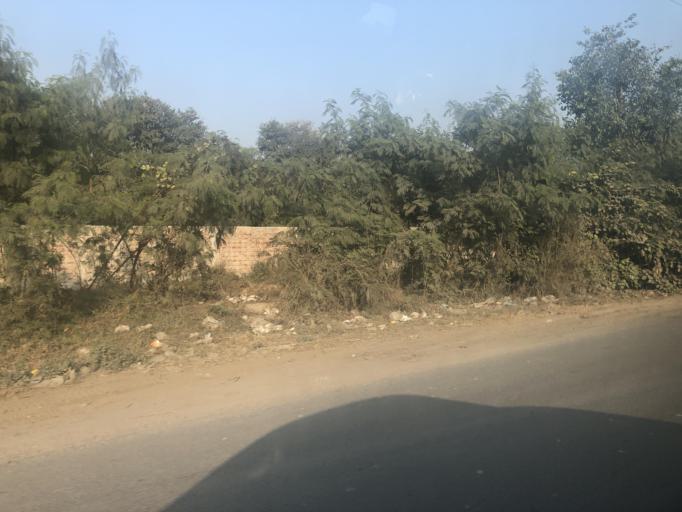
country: IN
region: Haryana
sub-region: Gurgaon
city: Gurgaon
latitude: 28.5389
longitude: 77.0314
